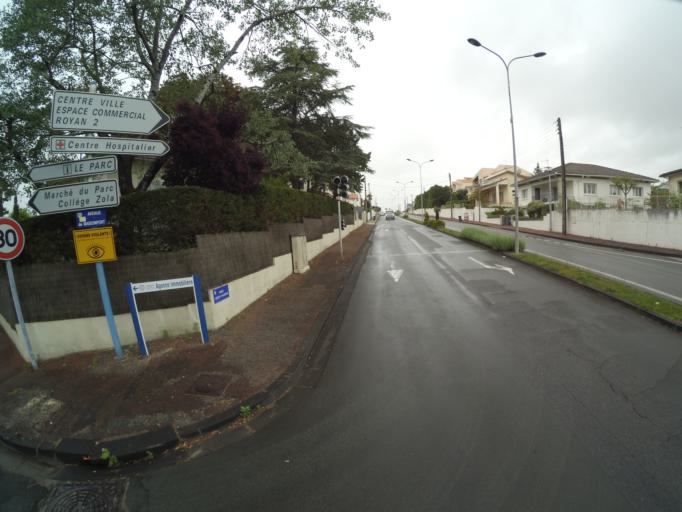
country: FR
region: Poitou-Charentes
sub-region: Departement de la Charente-Maritime
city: Saint-Georges-de-Didonne
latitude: 45.6193
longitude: -1.0070
